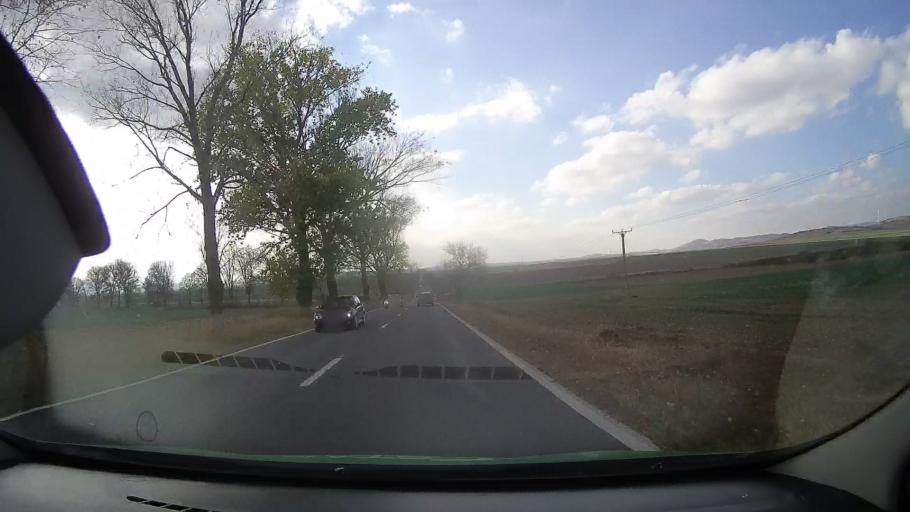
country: RO
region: Tulcea
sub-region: Comuna Nalbant
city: Nalbant
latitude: 45.0657
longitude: 28.6449
